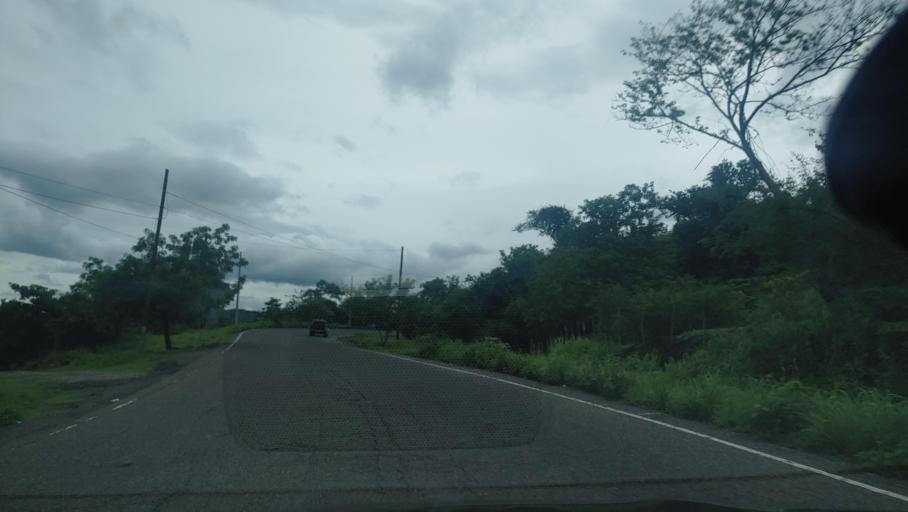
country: HN
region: Choluteca
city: Santa Ana de Yusguare
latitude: 13.3733
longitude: -87.0658
